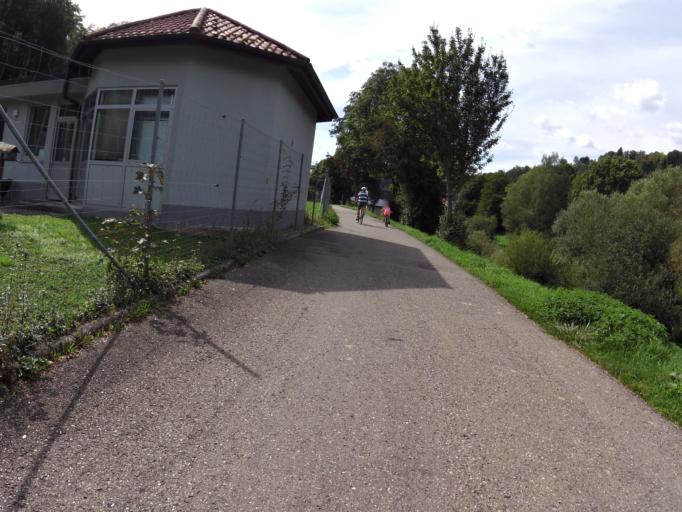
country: DE
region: Baden-Wuerttemberg
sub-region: Freiburg Region
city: Sulz am Neckar
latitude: 48.3682
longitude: 8.6443
